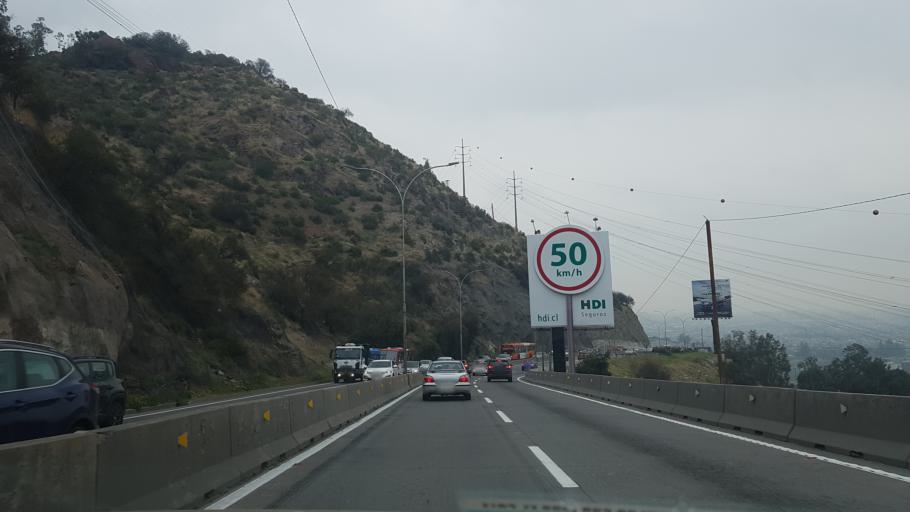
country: CL
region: Santiago Metropolitan
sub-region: Provincia de Santiago
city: Villa Presidente Frei, Nunoa, Santiago, Chile
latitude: -33.3900
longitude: -70.6037
